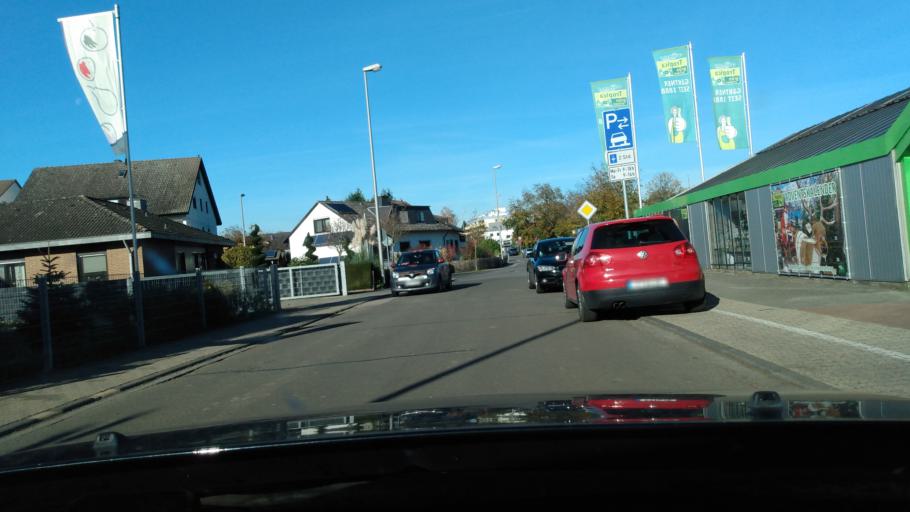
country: DE
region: Hesse
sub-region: Regierungsbezirk Darmstadt
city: Hattersheim
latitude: 50.0805
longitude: 8.4772
